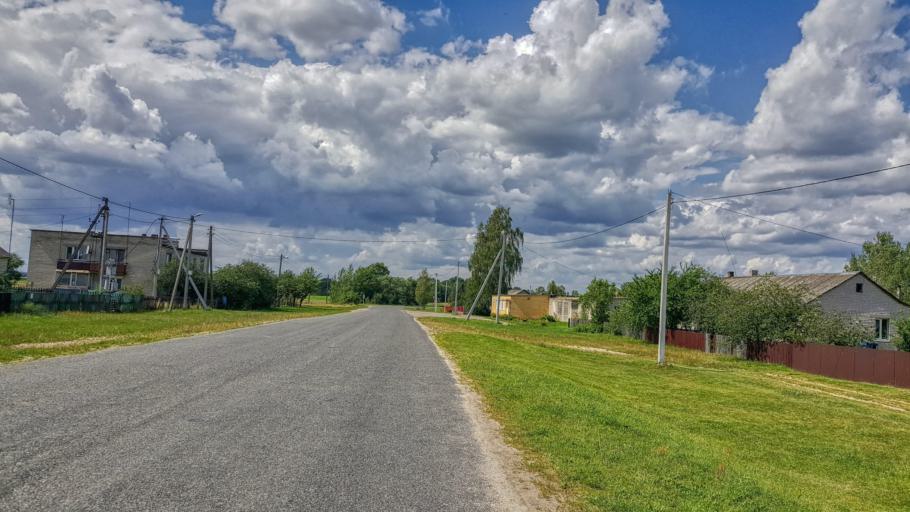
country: BY
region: Brest
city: Kamyanyets
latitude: 52.4138
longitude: 23.8893
